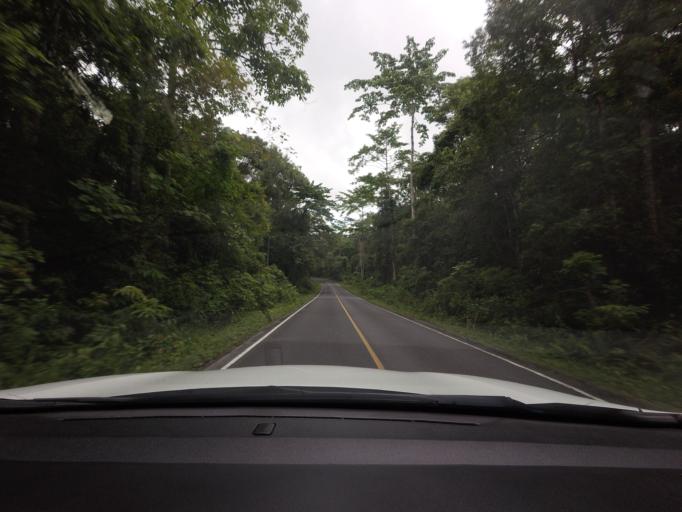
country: TH
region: Nakhon Nayok
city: Nakhon Nayok
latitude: 14.3564
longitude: 101.3447
